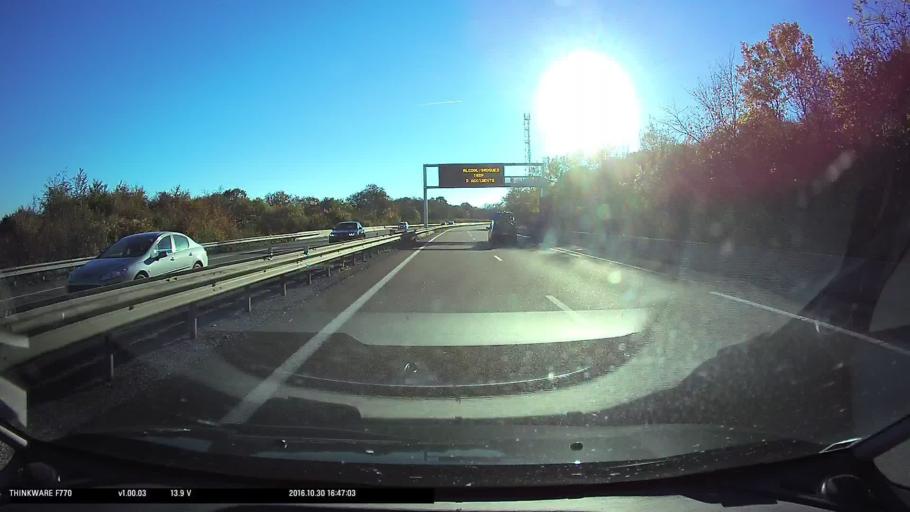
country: FR
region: Franche-Comte
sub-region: Departement du Doubs
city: Chatillon-le-Duc
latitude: 47.2904
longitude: 6.0143
